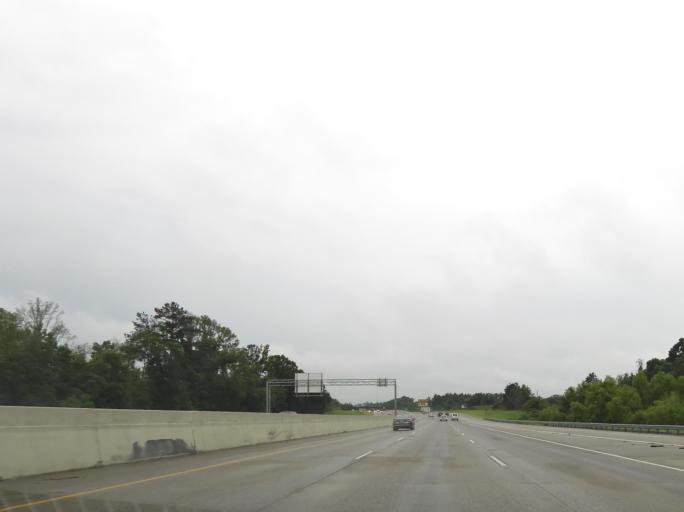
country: US
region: Georgia
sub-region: Crisp County
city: Cordele
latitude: 31.9317
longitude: -83.7472
